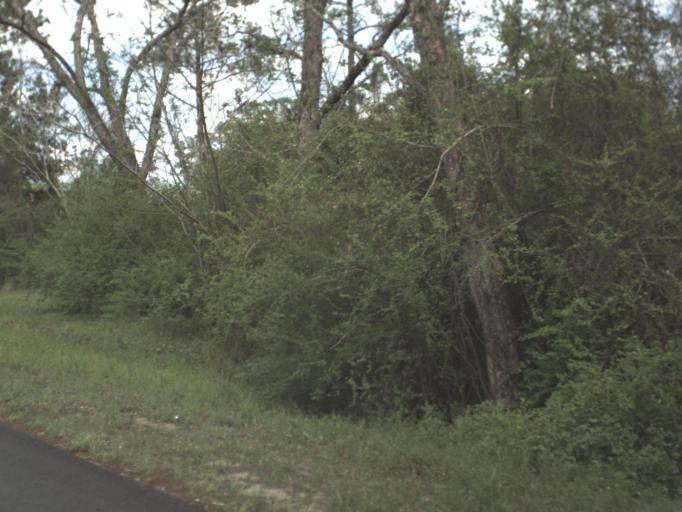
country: US
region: Alabama
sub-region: Covington County
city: Florala
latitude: 30.9483
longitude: -86.4772
